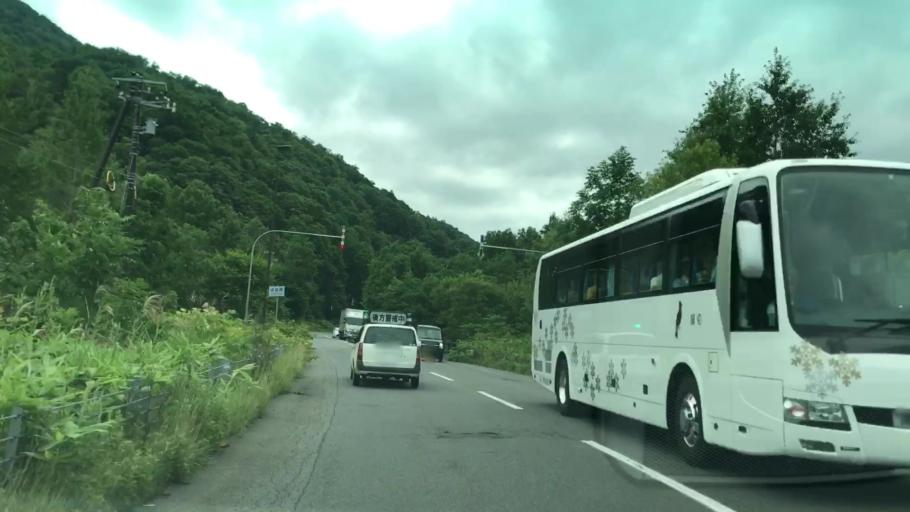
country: JP
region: Hokkaido
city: Yoichi
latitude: 43.0230
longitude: 140.8665
